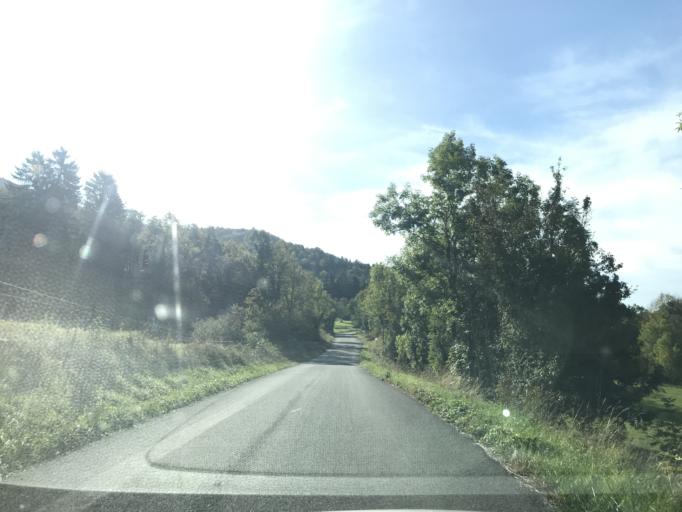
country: FR
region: Rhone-Alpes
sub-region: Departement de la Savoie
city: Novalaise
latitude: 45.6479
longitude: 5.7916
